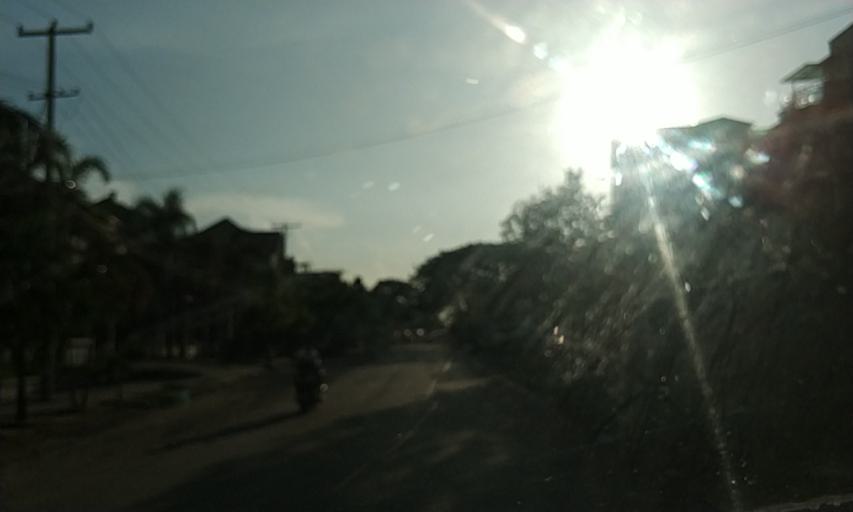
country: MM
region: Mandalay
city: Mandalay
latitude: 21.9700
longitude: 96.0991
